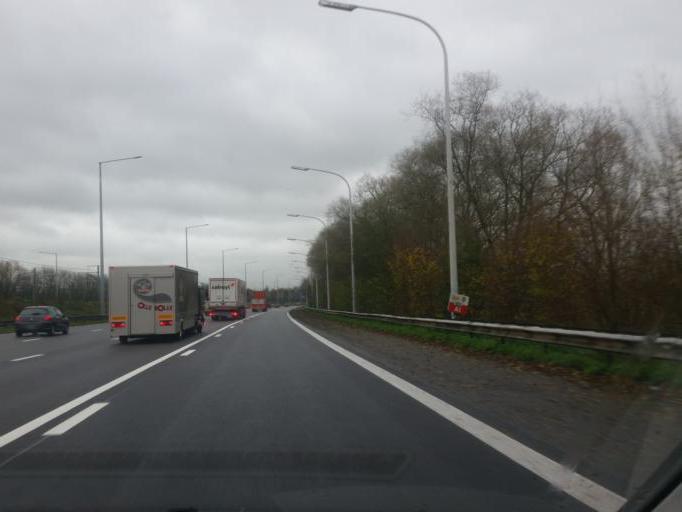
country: BE
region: Flanders
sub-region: Provincie Vlaams-Brabant
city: Zemst
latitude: 50.9716
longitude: 4.4900
